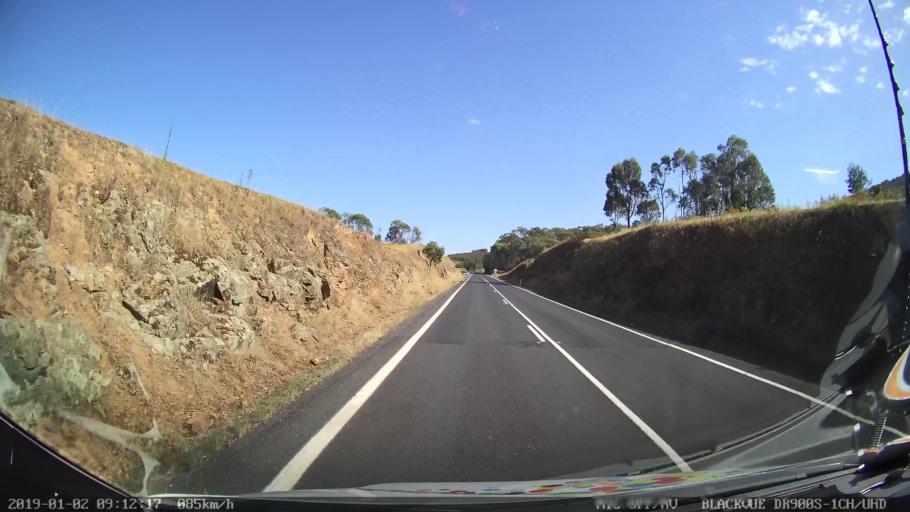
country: AU
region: New South Wales
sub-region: Tumut Shire
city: Tumut
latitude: -35.5024
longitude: 148.2728
